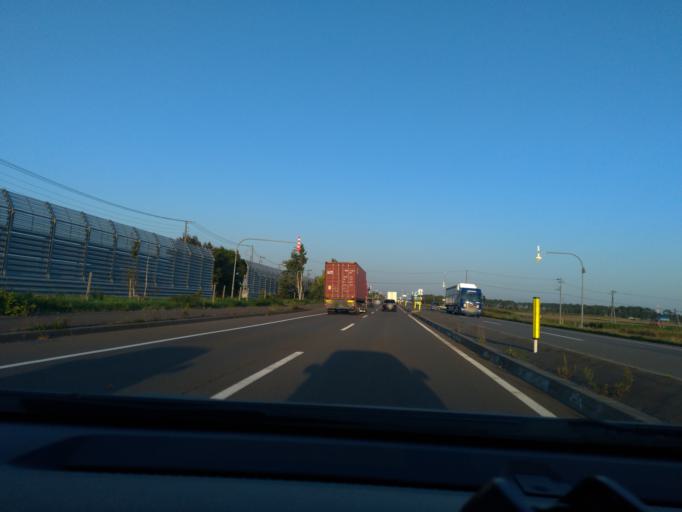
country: JP
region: Hokkaido
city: Tobetsu
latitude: 43.1798
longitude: 141.4684
